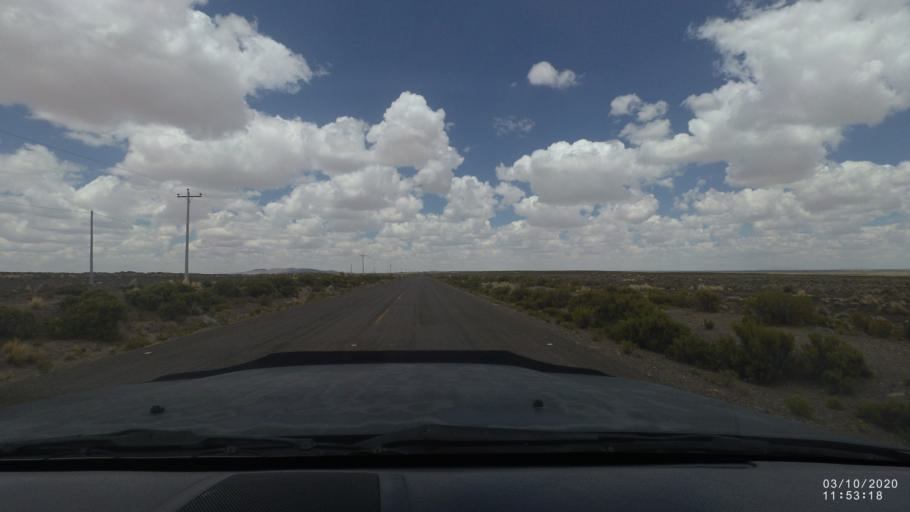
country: BO
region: Oruro
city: Poopo
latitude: -18.4752
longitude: -67.6034
